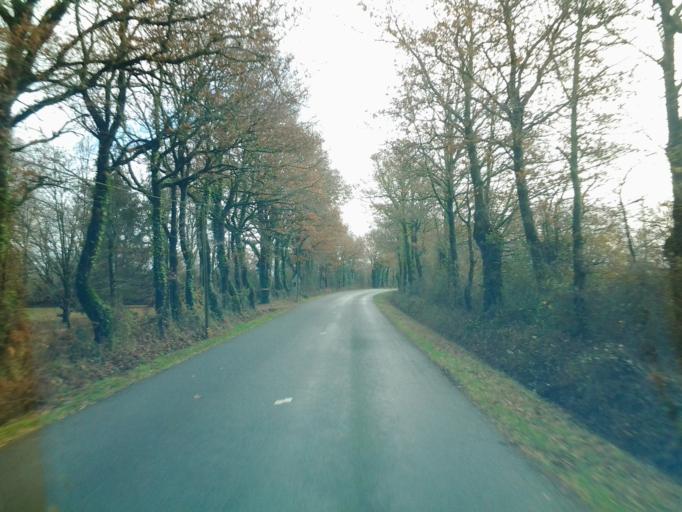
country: FR
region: Pays de la Loire
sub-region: Departement de la Vendee
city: Saint-Florent-des-Bois
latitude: 46.6343
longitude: -1.3357
